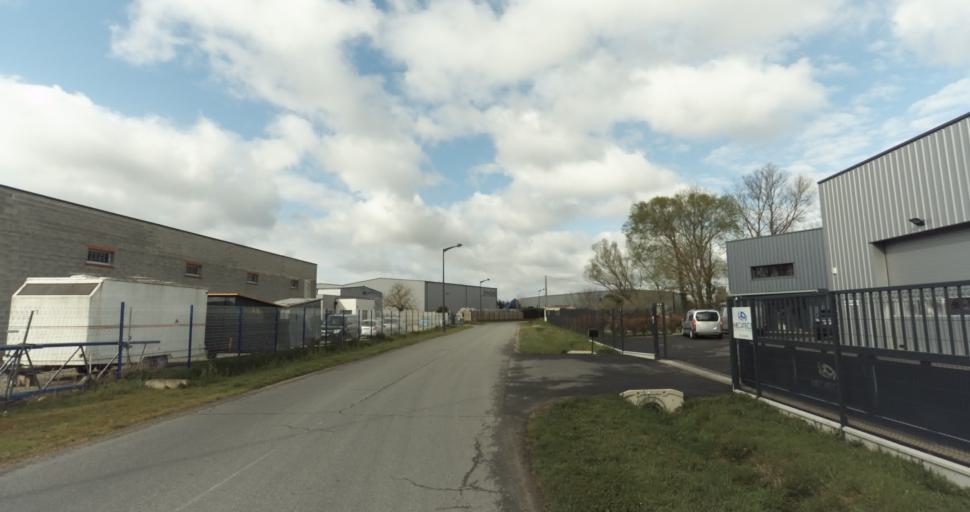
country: FR
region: Midi-Pyrenees
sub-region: Departement de la Haute-Garonne
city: Auterive
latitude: 43.3646
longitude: 1.4494
